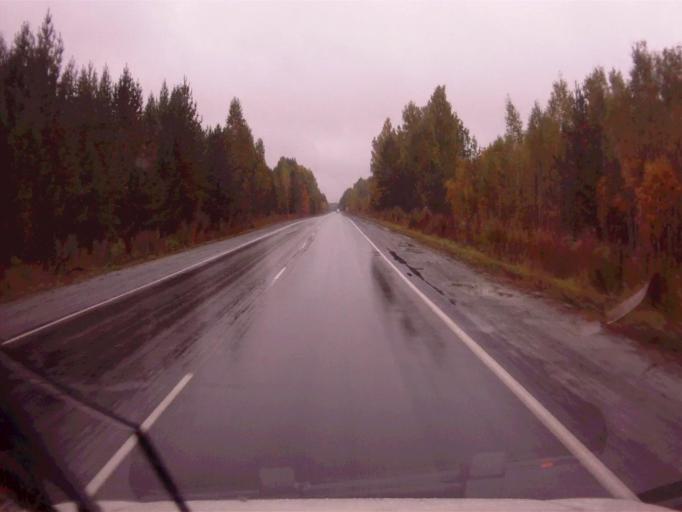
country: RU
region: Chelyabinsk
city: Tayginka
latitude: 55.5412
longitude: 60.6466
